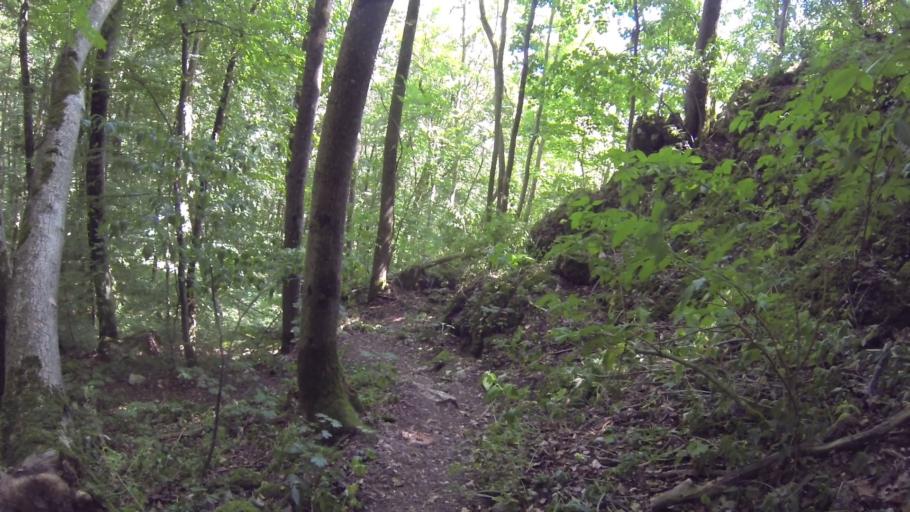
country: DE
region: Baden-Wuerttemberg
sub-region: Regierungsbezirk Stuttgart
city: Herbrechtingen
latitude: 48.6069
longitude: 10.1574
